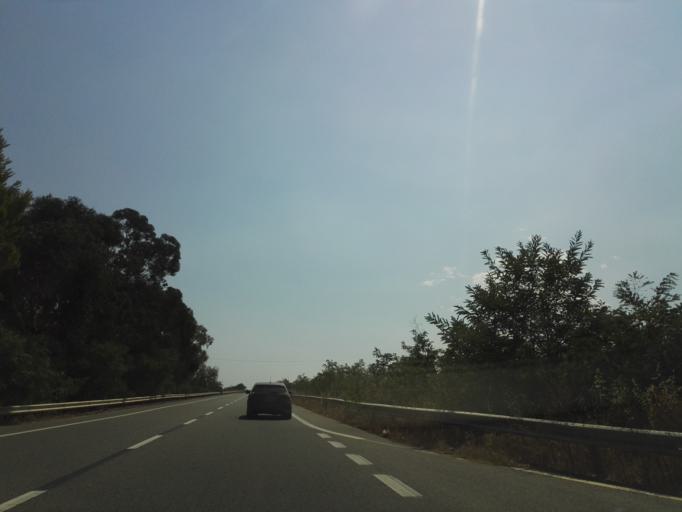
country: IT
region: Calabria
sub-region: Provincia di Reggio Calabria
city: Riace Marina
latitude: 38.3751
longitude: 16.5113
